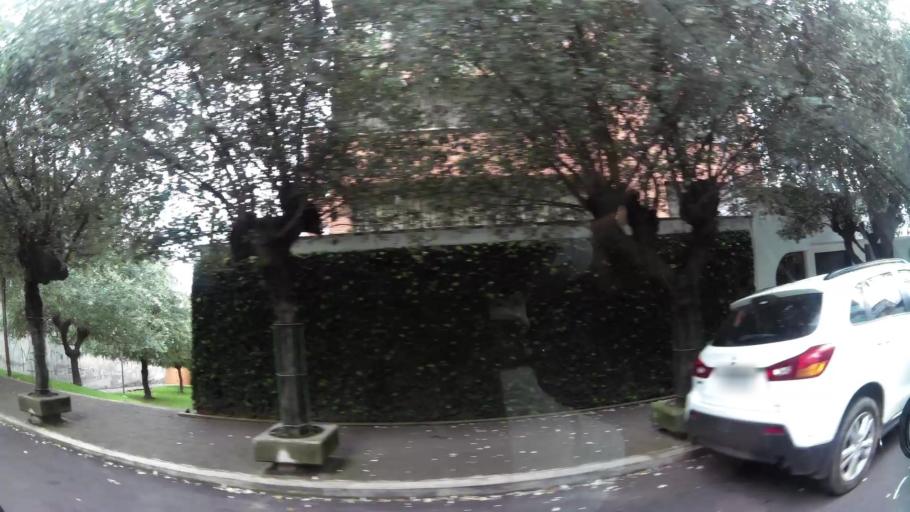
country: EC
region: Pichincha
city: Quito
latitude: -0.1681
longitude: -78.4963
